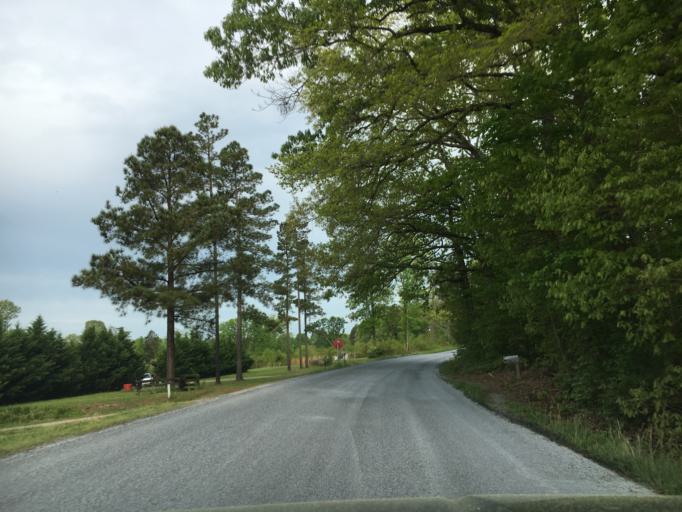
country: US
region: Virginia
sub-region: Campbell County
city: Brookneal
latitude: 36.9467
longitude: -78.9605
